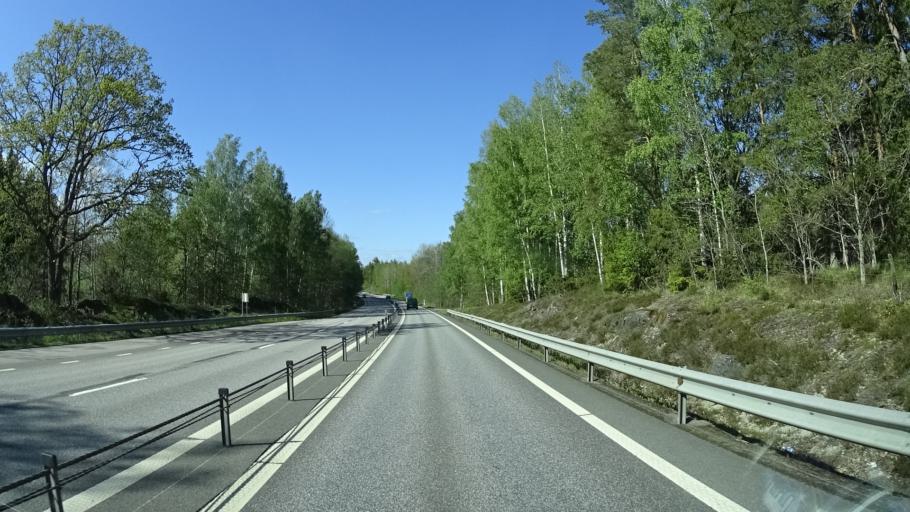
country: SE
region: OEstergoetland
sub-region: Valdemarsviks Kommun
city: Valdemarsvik
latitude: 58.1085
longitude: 16.5427
